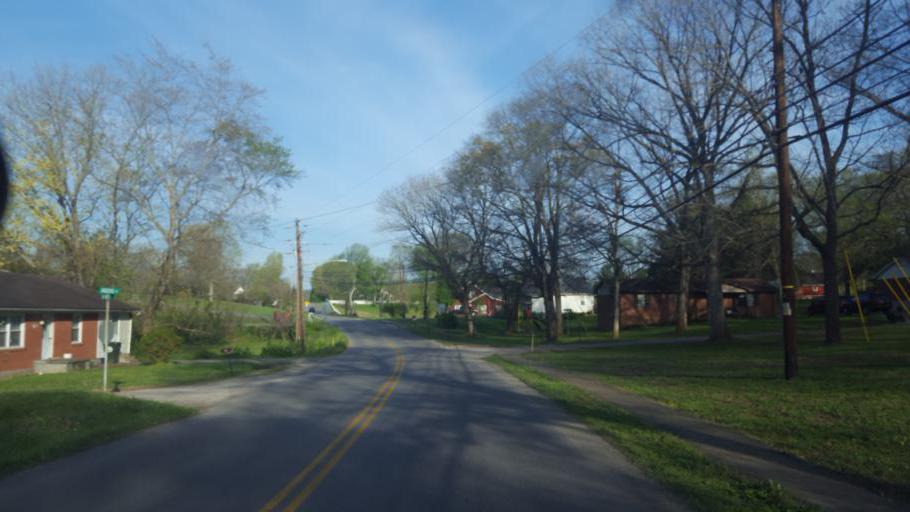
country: US
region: Kentucky
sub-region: Hart County
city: Munfordville
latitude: 37.2724
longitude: -85.8959
